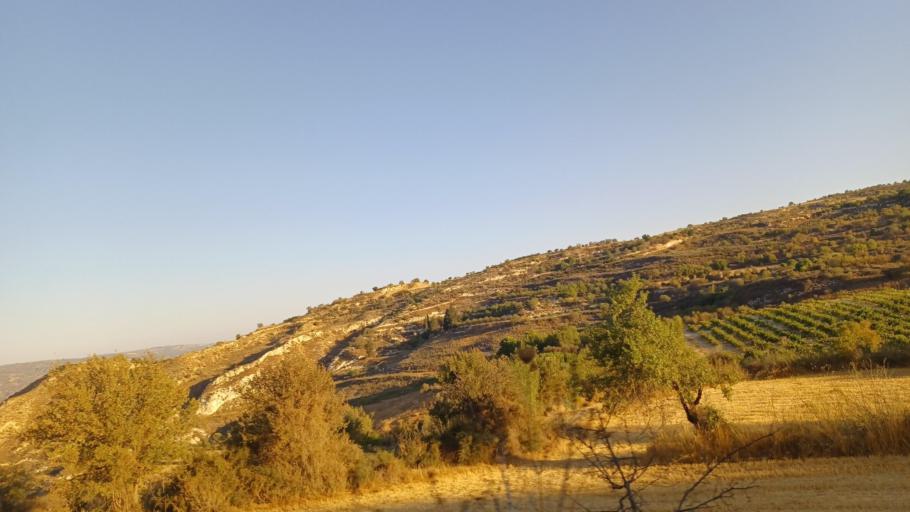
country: CY
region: Pafos
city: Mesogi
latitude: 34.9063
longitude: 32.5206
